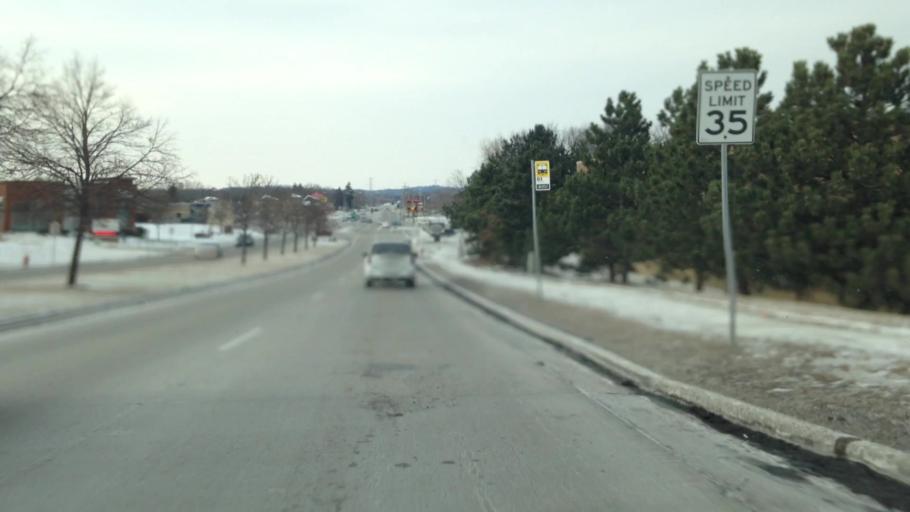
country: US
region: Wisconsin
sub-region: Waukesha County
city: Menomonee Falls
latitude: 43.1901
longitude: -88.1333
